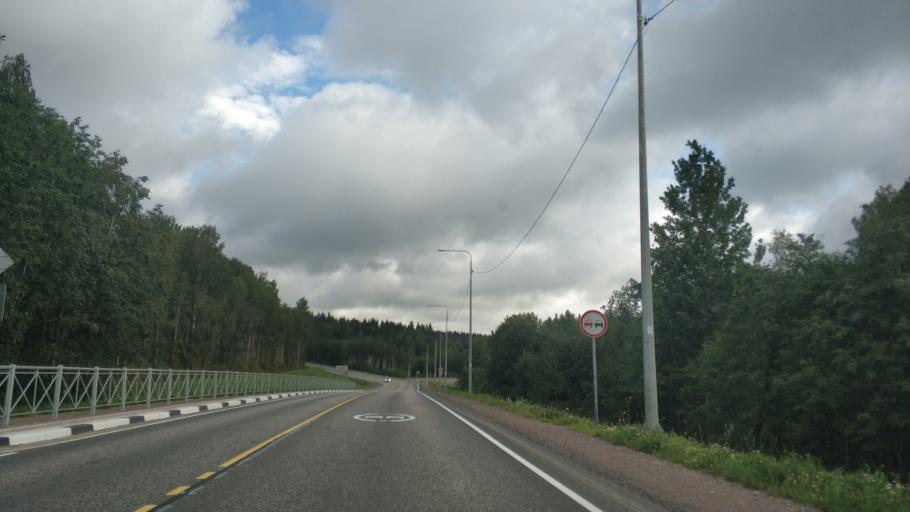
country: RU
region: Republic of Karelia
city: Khelyulya
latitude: 61.8225
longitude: 30.6346
